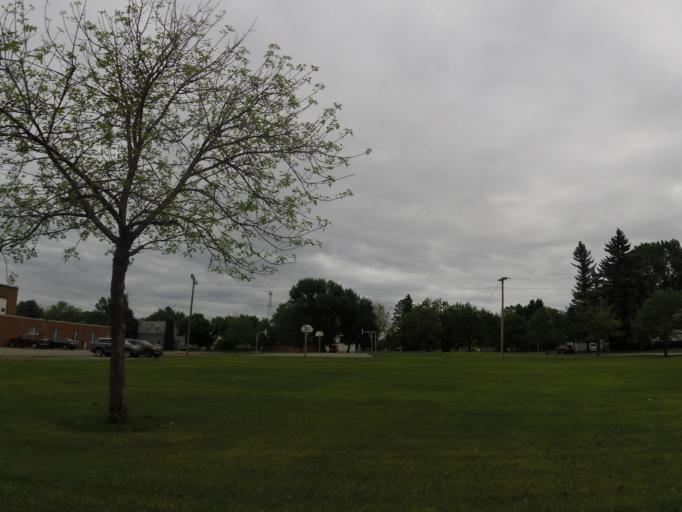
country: US
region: North Dakota
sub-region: Walsh County
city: Grafton
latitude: 48.6184
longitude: -97.4520
